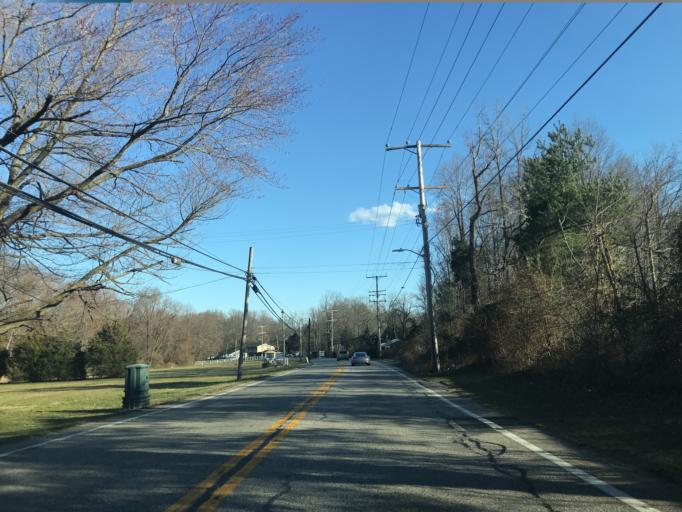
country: US
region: Maryland
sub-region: Anne Arundel County
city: Selby-on-the-Bay
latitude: 38.9089
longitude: -76.5401
